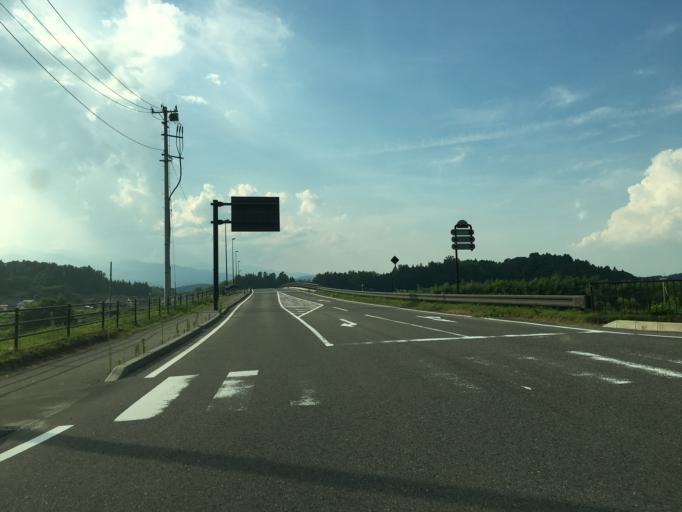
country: JP
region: Fukushima
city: Nihommatsu
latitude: 37.5526
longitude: 140.4365
